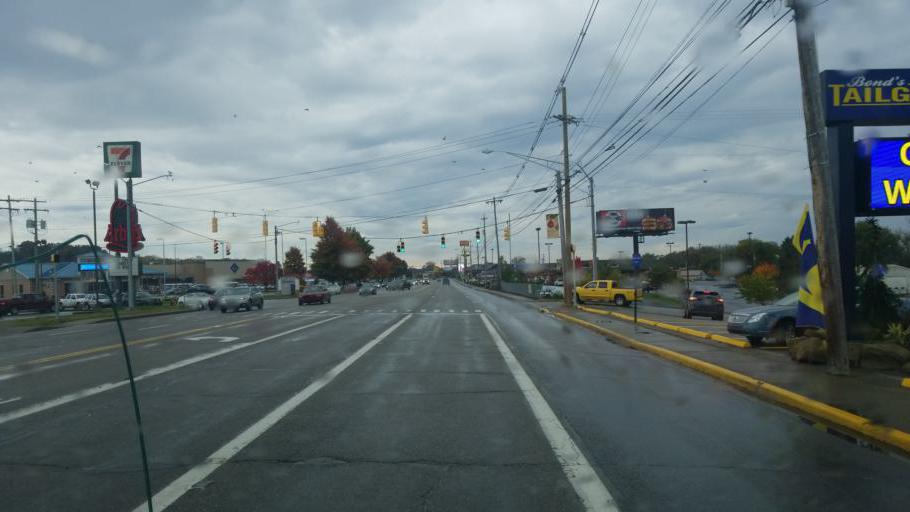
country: US
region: West Virginia
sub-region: Wood County
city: Vienna
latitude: 39.3124
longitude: -81.5533
